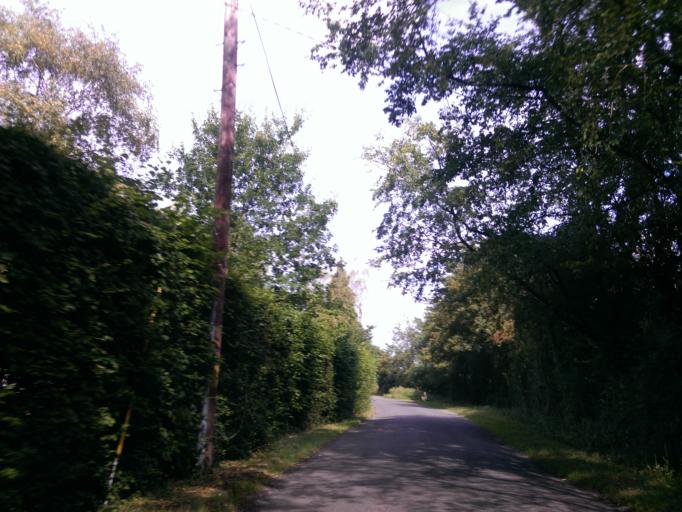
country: GB
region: England
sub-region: Essex
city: Sible Hedingham
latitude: 51.9691
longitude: 0.6224
